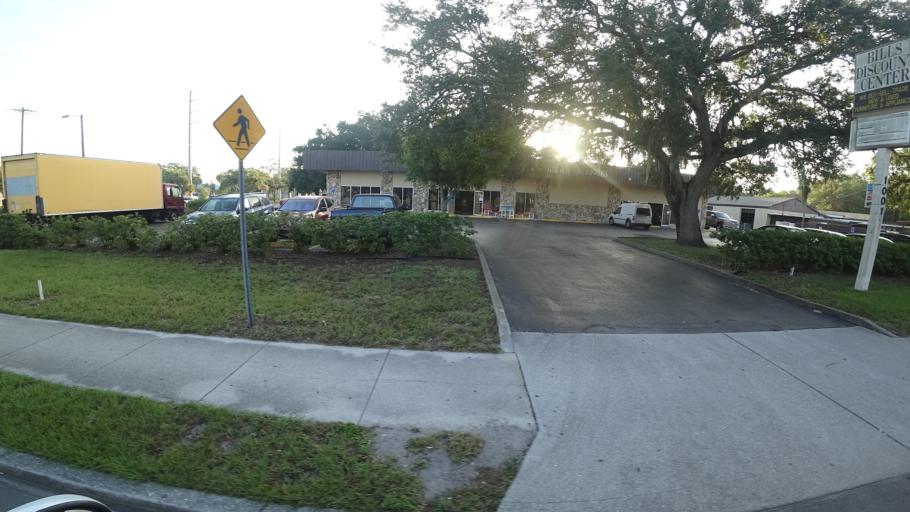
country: US
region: Florida
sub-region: Manatee County
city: Bradenton
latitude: 27.4914
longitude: -82.5712
